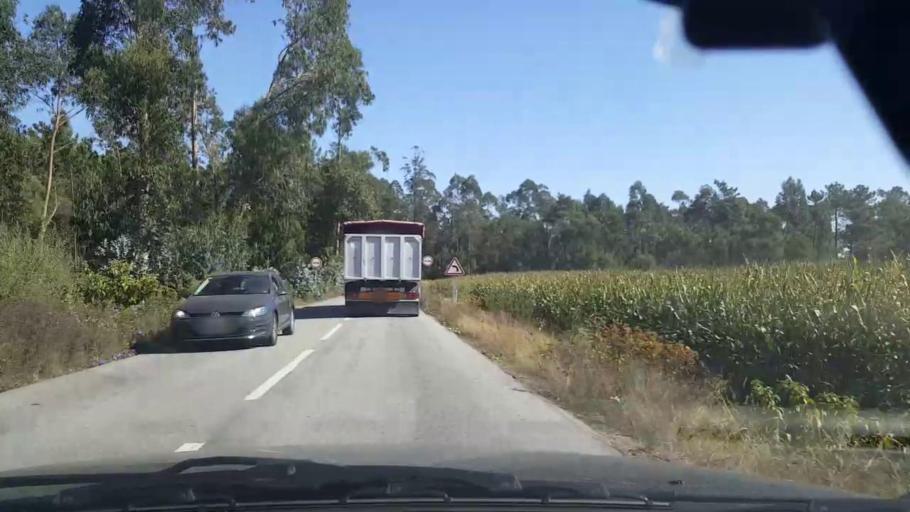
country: PT
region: Braga
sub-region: Vila Nova de Famalicao
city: Ribeirao
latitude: 41.3609
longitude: -8.6275
